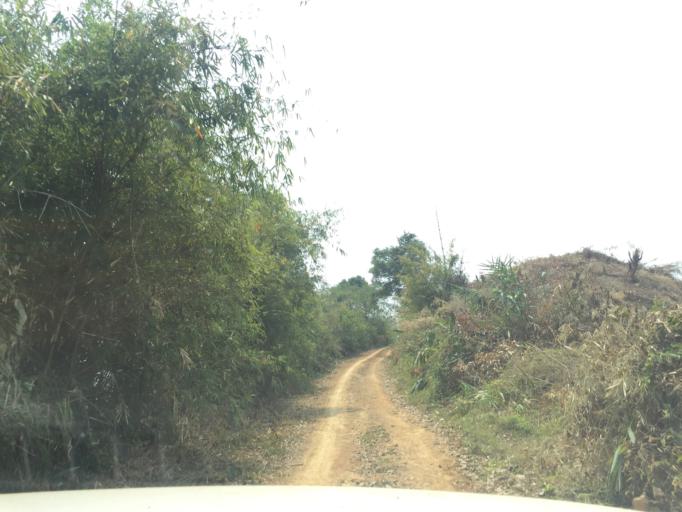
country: LA
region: Loungnamtha
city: Muang Nale
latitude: 20.6247
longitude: 101.6242
